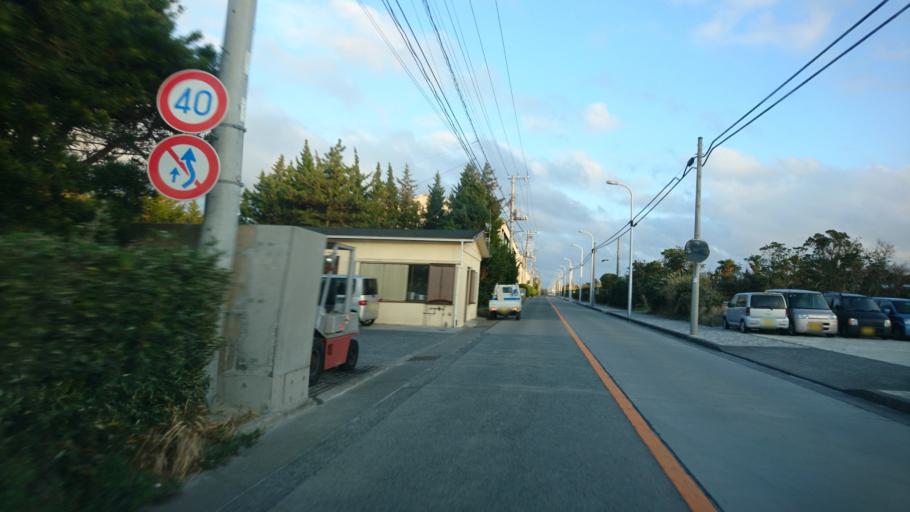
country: JP
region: Shizuoka
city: Shimoda
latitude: 34.3720
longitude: 139.2616
